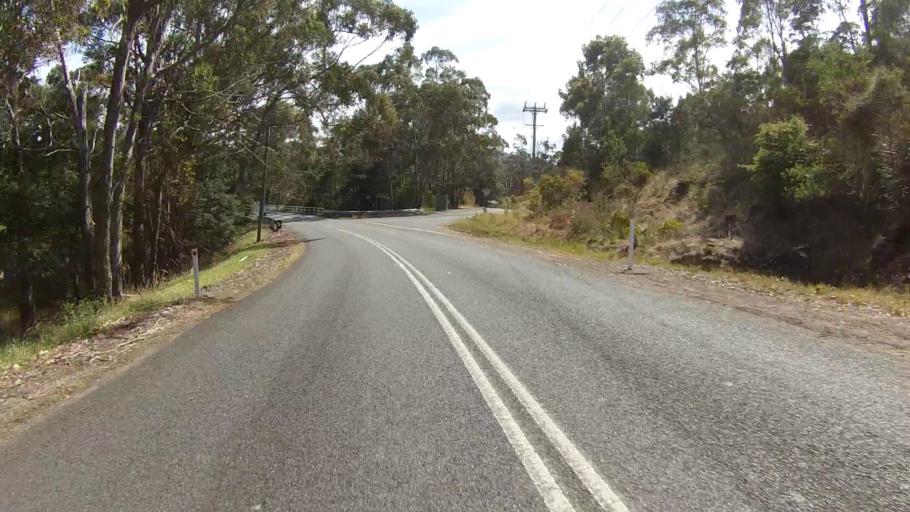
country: AU
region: Tasmania
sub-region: Huon Valley
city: Cygnet
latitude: -43.2420
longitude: 147.1511
